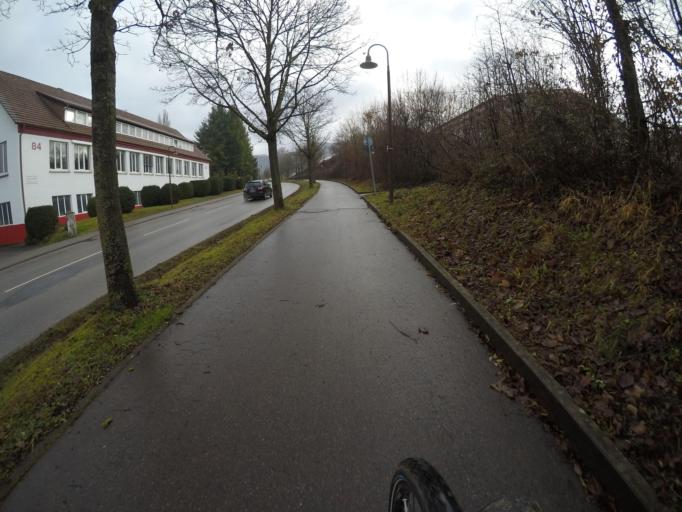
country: DE
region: Baden-Wuerttemberg
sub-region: Regierungsbezirk Stuttgart
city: Beuren
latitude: 48.5736
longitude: 9.3938
